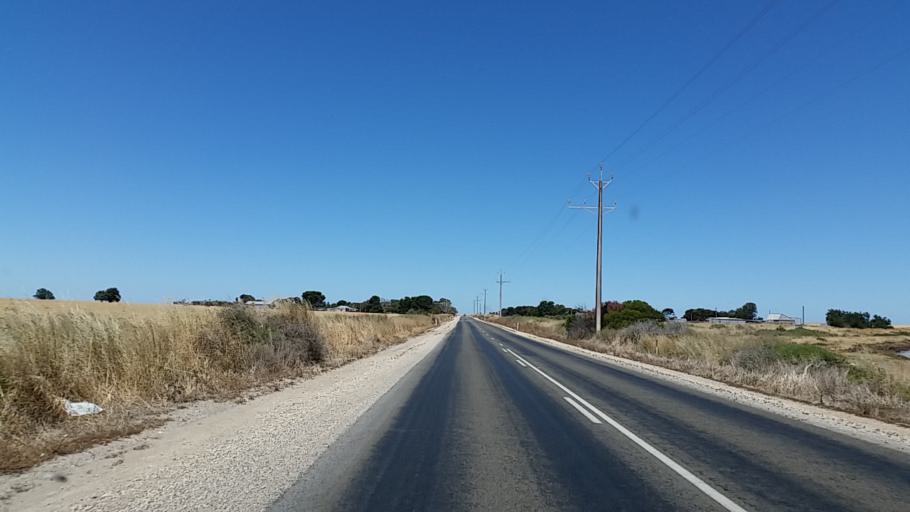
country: AU
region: South Australia
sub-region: Yorke Peninsula
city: Honiton
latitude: -35.0138
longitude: 137.6267
